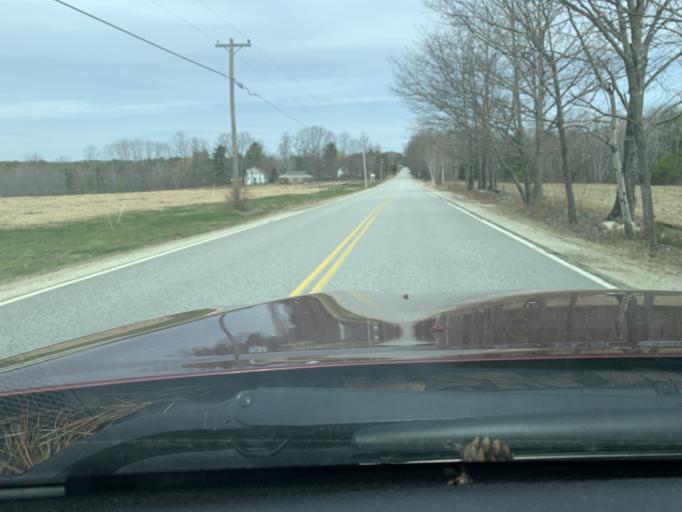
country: US
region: Maine
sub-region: Cumberland County
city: Raymond
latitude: 43.9586
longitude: -70.3891
